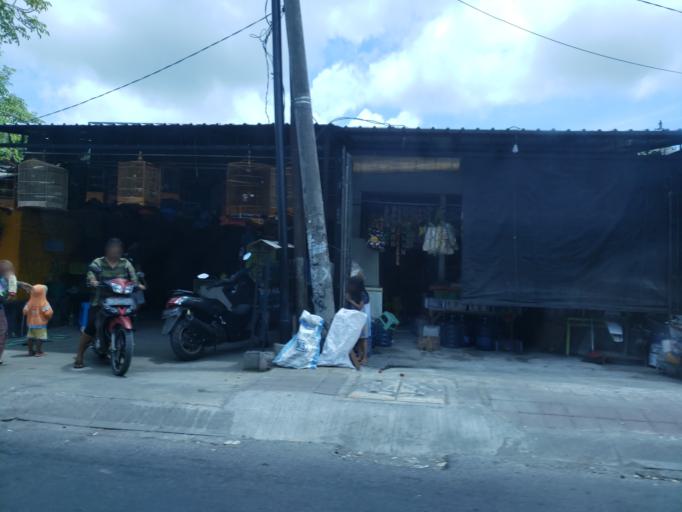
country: ID
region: Bali
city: Jimbaran
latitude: -8.8144
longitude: 115.1569
